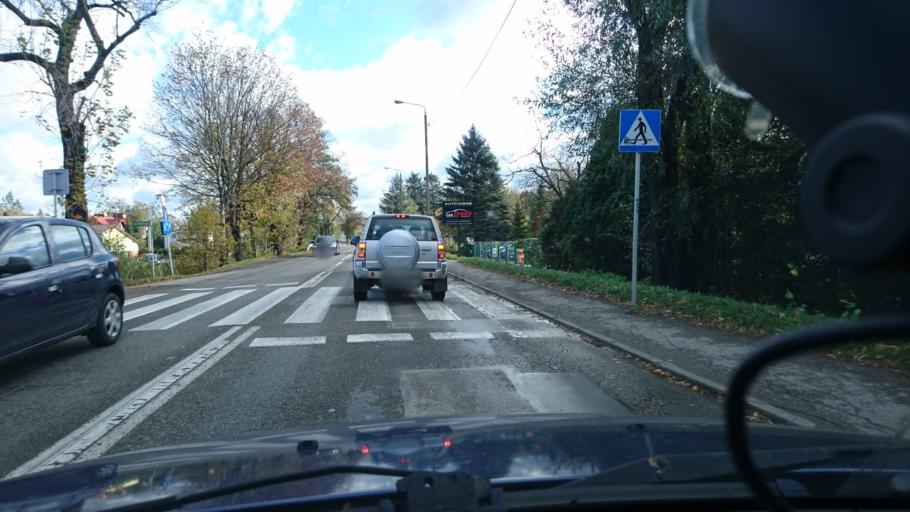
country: PL
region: Silesian Voivodeship
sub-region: Powiat bielski
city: Jaworze
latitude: 49.8077
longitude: 18.9792
